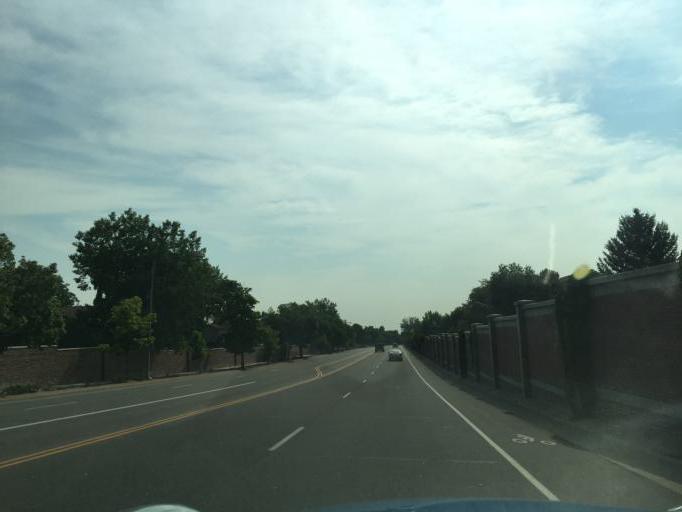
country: US
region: Colorado
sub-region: Adams County
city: Westminster
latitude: 39.8272
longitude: -105.0673
